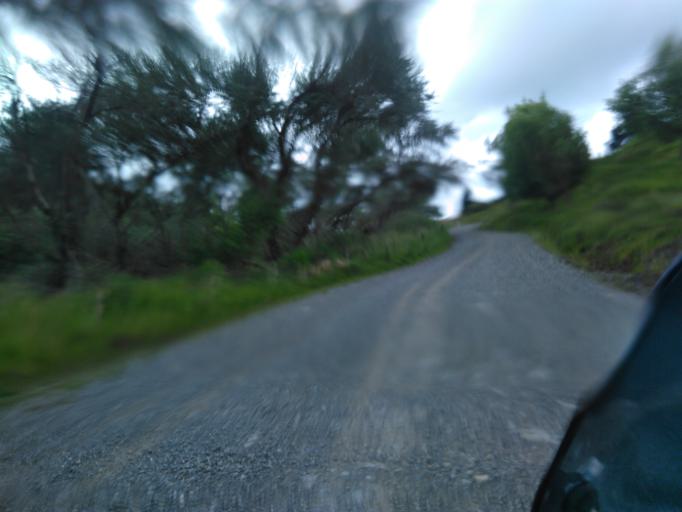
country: NZ
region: Gisborne
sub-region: Gisborne District
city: Gisborne
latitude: -38.0707
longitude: 178.0451
